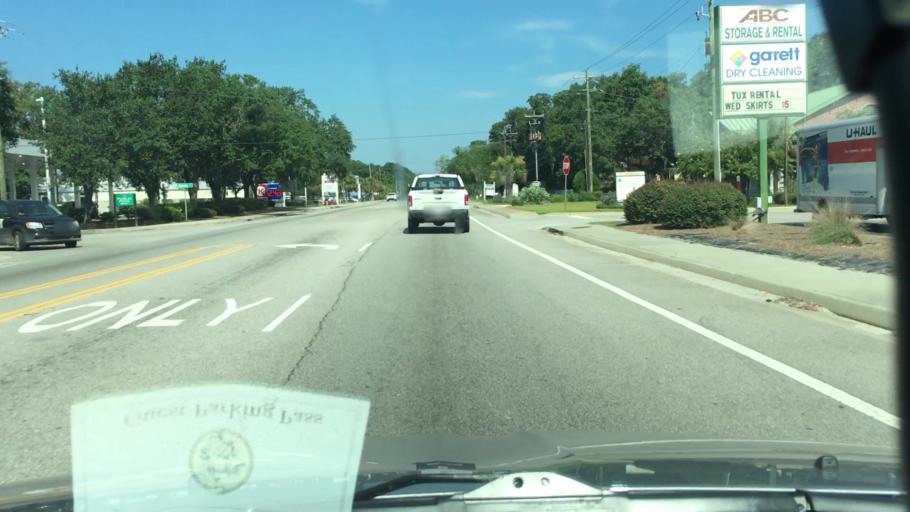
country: US
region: South Carolina
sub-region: Beaufort County
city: Beaufort
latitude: 32.4158
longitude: -80.6542
